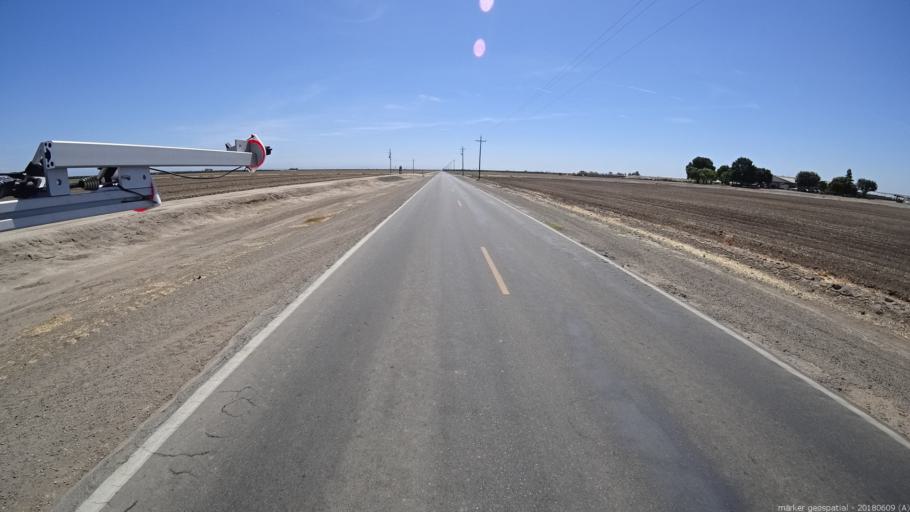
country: US
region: California
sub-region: Madera County
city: Fairmead
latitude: 36.9528
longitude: -120.2488
